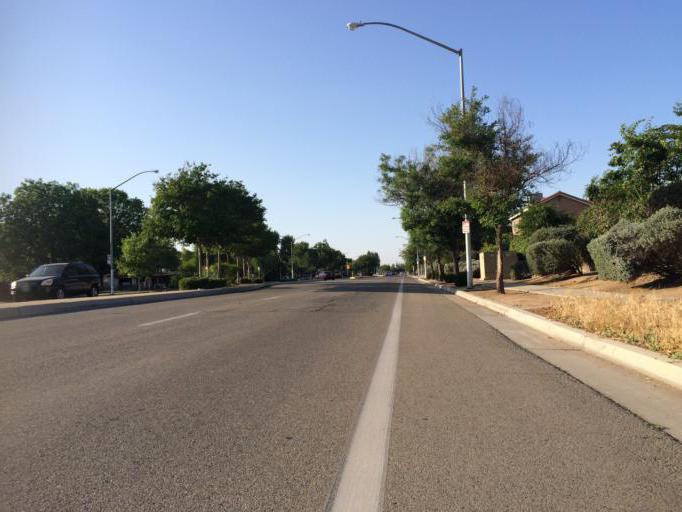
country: US
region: California
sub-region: Fresno County
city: Sunnyside
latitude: 36.7596
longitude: -119.7182
